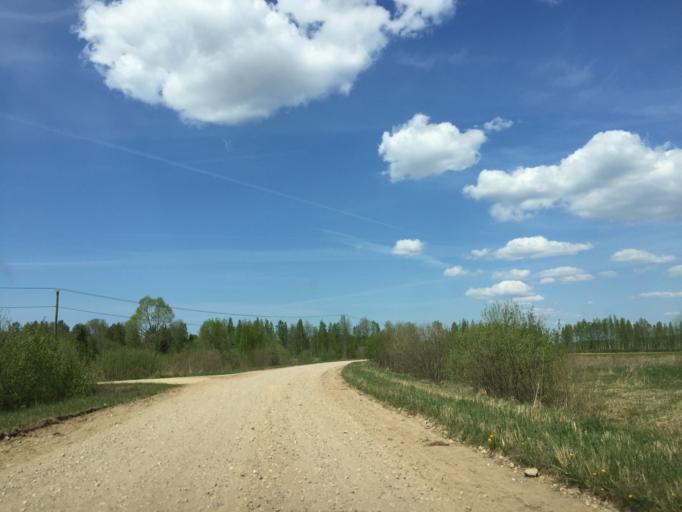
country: LV
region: Limbazu Rajons
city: Limbazi
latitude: 57.3887
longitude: 24.5735
